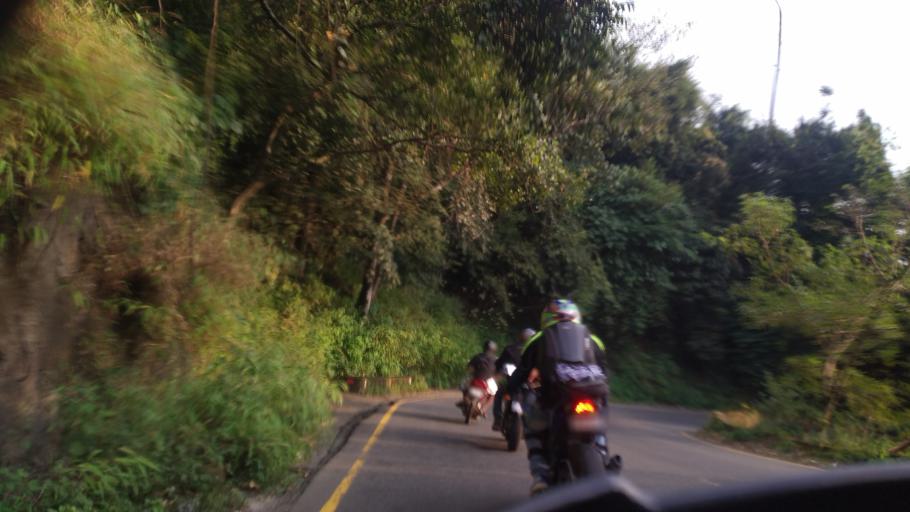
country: IN
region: Kerala
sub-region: Wayanad
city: Kalpetta
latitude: 11.5148
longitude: 76.0152
